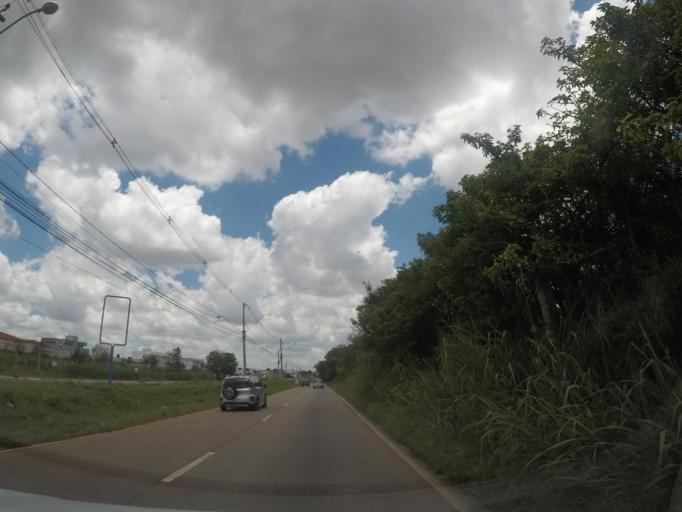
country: BR
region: Sao Paulo
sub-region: Hortolandia
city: Hortolandia
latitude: -22.8276
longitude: -47.2083
